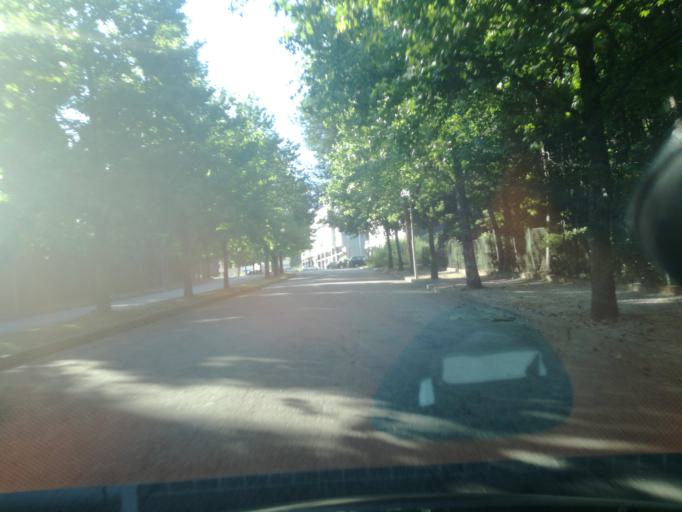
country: PT
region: Porto
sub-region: Maia
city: Gemunde
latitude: 41.2490
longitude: -8.6544
